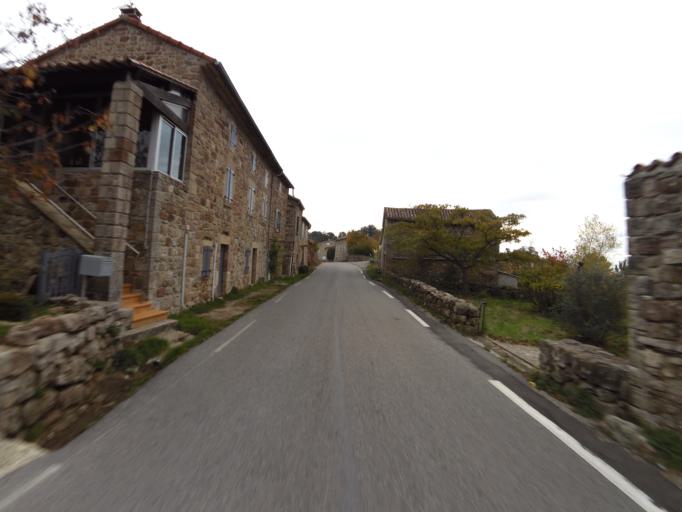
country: FR
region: Rhone-Alpes
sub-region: Departement de l'Ardeche
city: Lablachere
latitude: 44.4857
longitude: 4.1544
